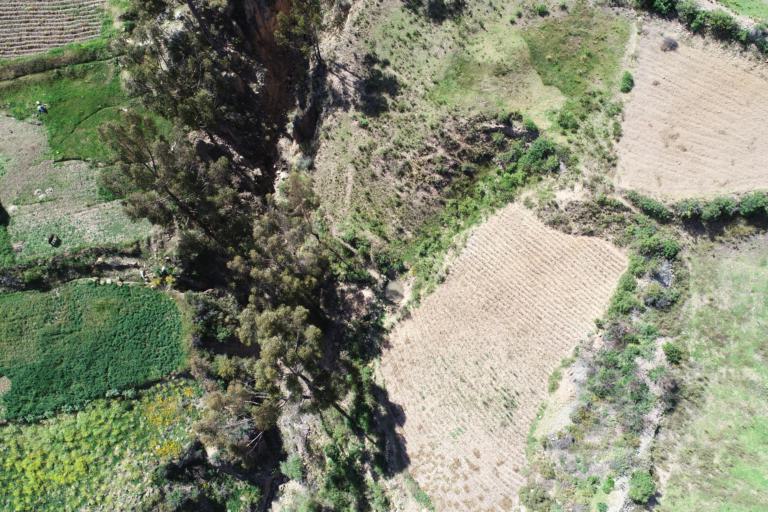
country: BO
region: La Paz
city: La Paz
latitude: -16.5521
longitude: -67.9876
